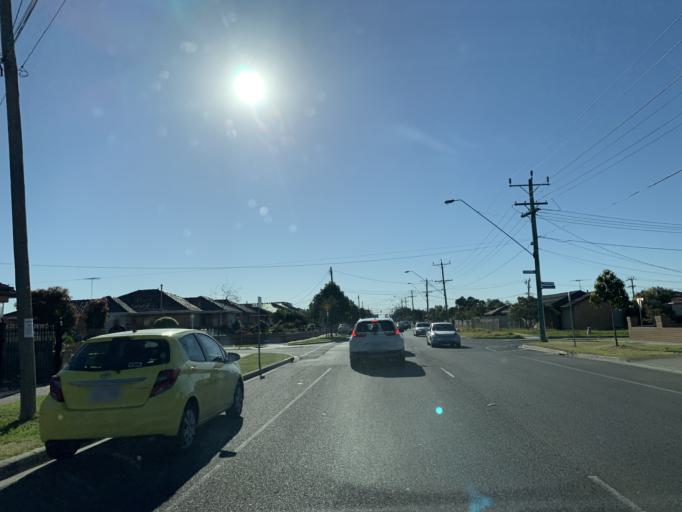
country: AU
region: Victoria
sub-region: Brimbank
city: St Albans
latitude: -37.7595
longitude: 144.8056
